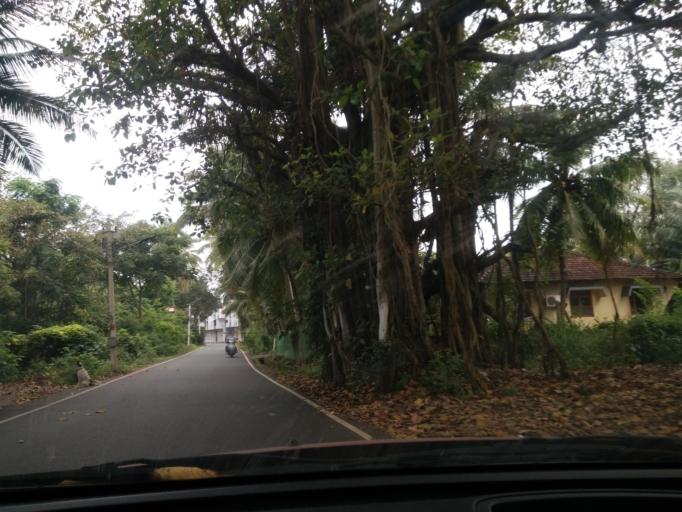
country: IN
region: Goa
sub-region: South Goa
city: Benaulim
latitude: 15.2686
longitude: 73.9287
